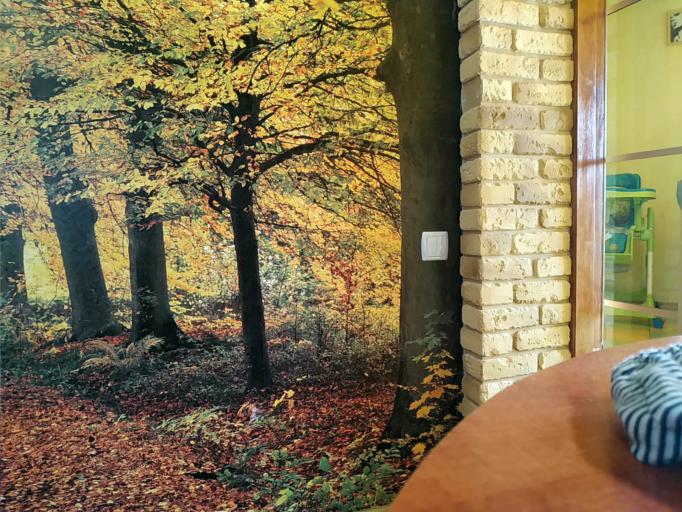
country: RU
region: Novgorod
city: Parfino
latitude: 57.7961
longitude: 31.6296
